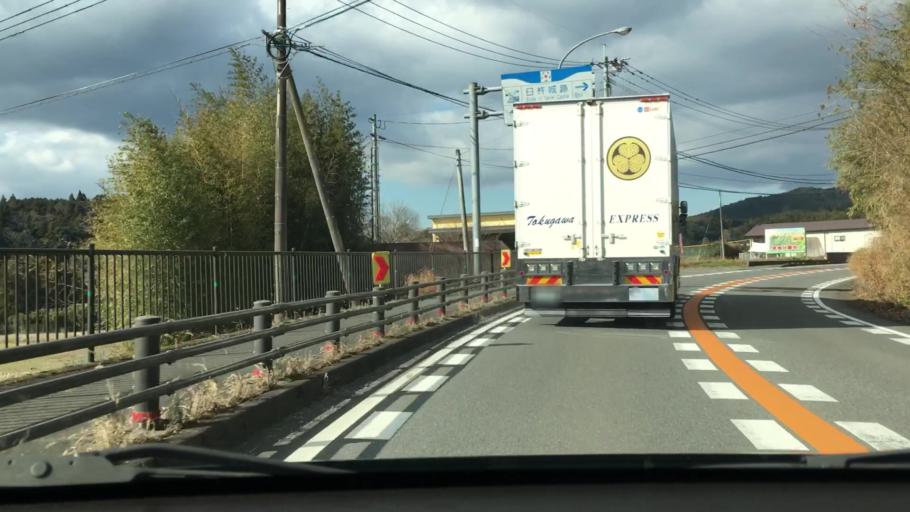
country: JP
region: Oita
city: Usuki
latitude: 33.0500
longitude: 131.6890
